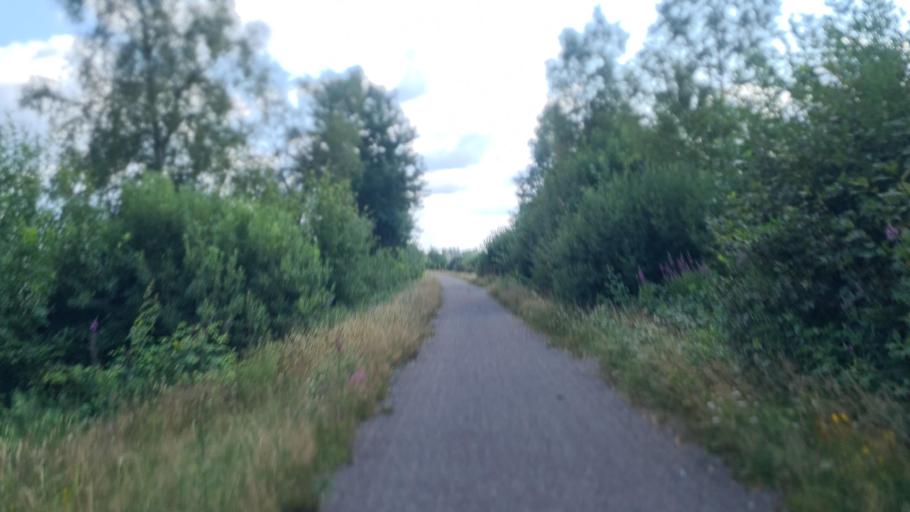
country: SE
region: Kronoberg
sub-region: Ljungby Kommun
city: Ljungby
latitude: 56.7907
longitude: 13.9058
